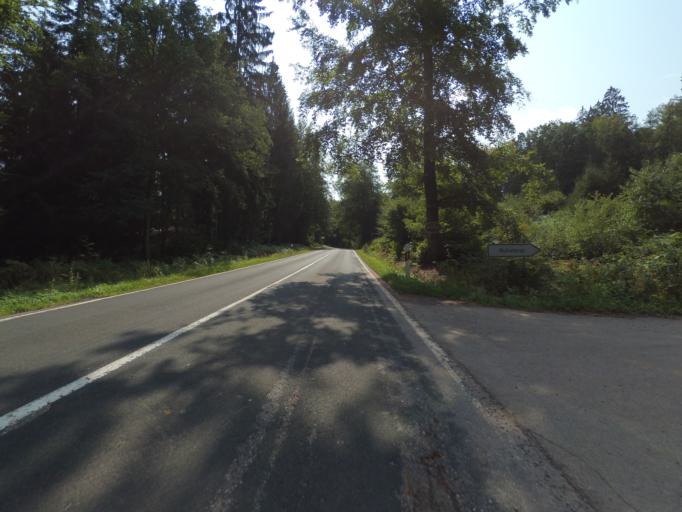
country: DE
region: Saarland
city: Britten
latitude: 49.5077
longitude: 6.6513
